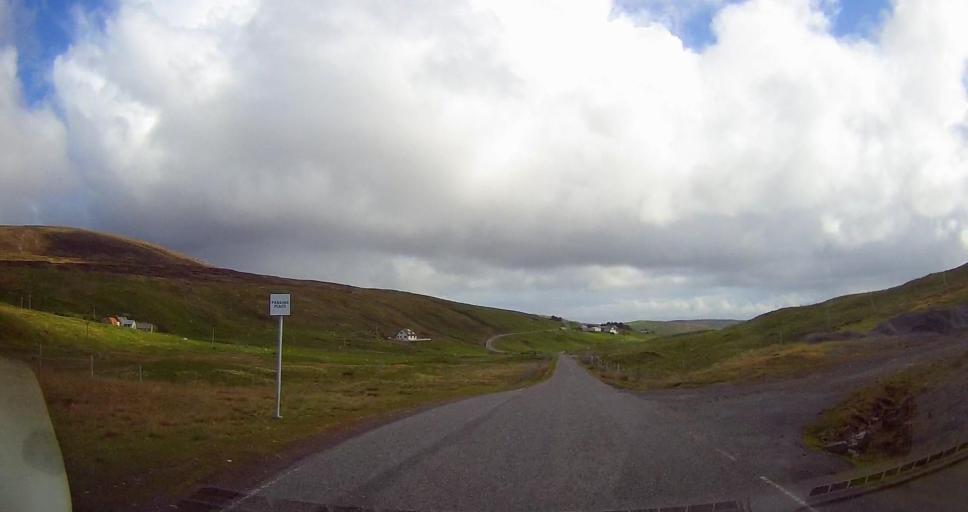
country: GB
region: Scotland
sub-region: Shetland Islands
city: Lerwick
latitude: 60.5214
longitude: -1.3764
